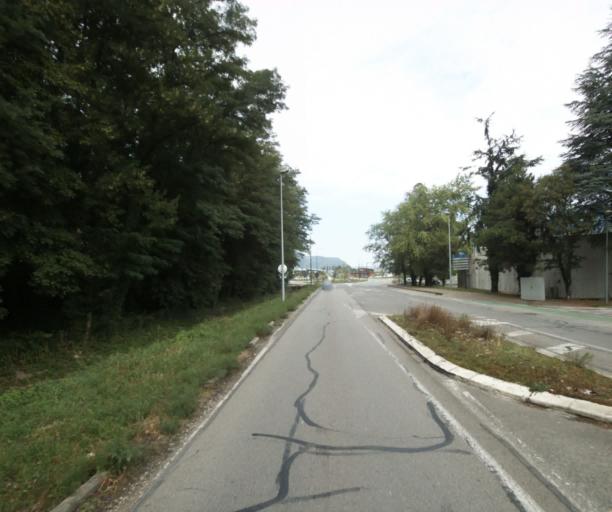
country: FR
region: Rhone-Alpes
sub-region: Departement de l'Isere
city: Fontanil-Cornillon
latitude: 45.2386
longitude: 5.6677
